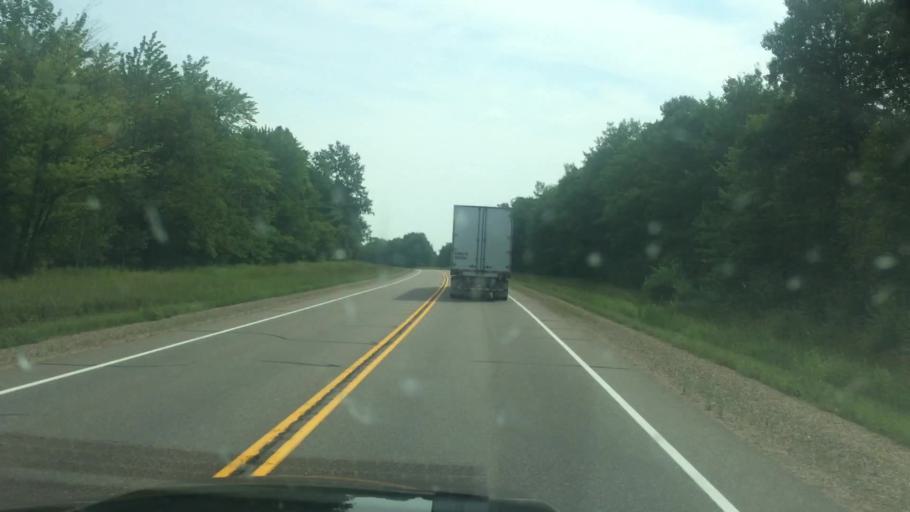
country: US
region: Wisconsin
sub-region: Langlade County
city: Antigo
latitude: 45.1440
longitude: -89.3020
